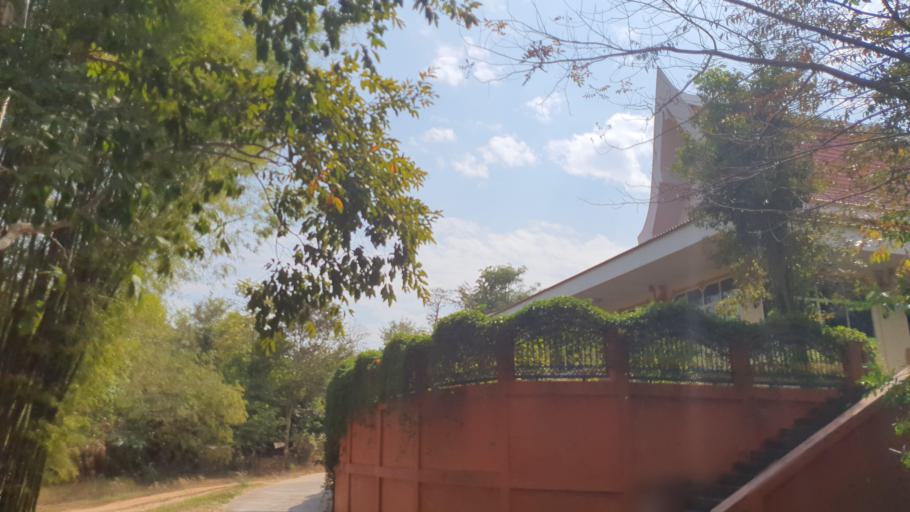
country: TH
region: Changwat Bueng Kan
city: Si Wilai
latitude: 18.2704
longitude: 103.7990
